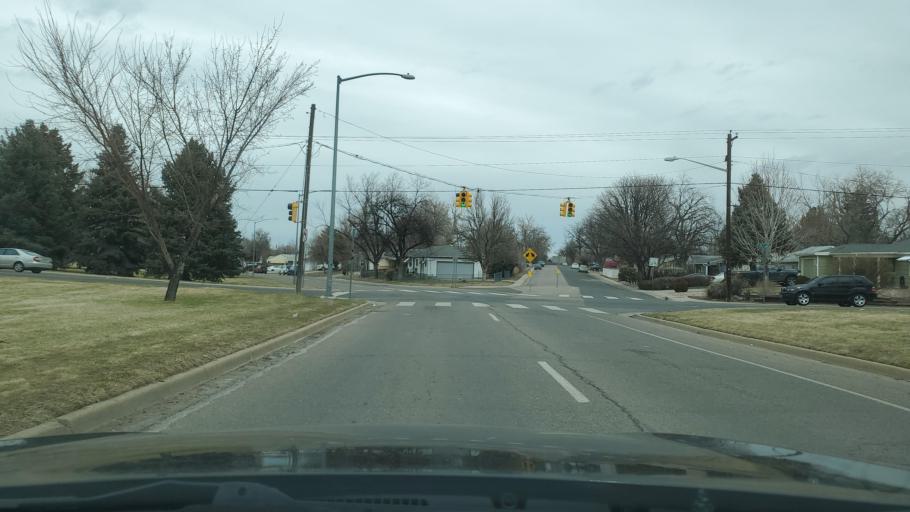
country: US
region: Colorado
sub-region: Adams County
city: Aurora
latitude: 39.7325
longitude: -104.8647
